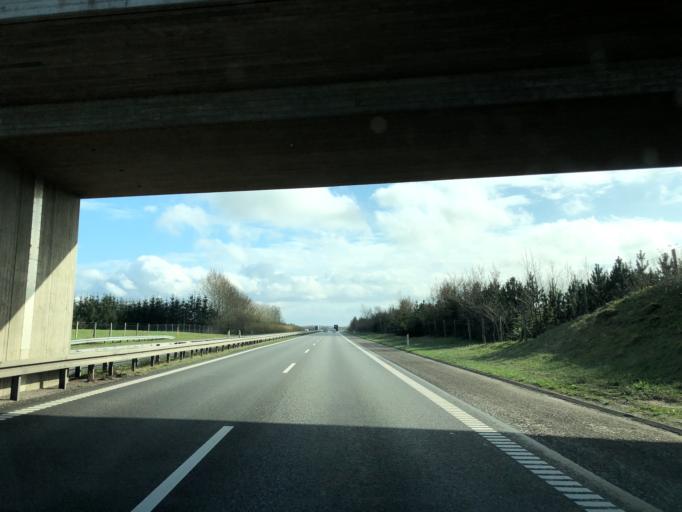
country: DK
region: North Denmark
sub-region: Hjorring Kommune
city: Vra
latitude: 57.3155
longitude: 10.0200
